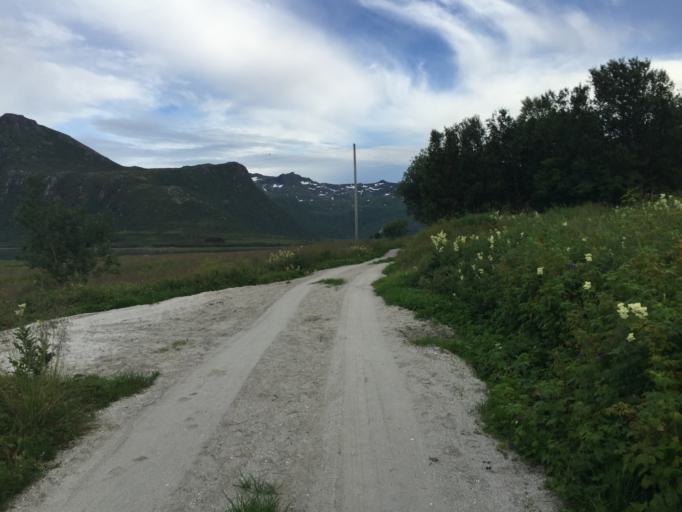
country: NO
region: Nordland
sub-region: Vagan
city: Kabelvag
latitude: 68.3288
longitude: 14.3962
